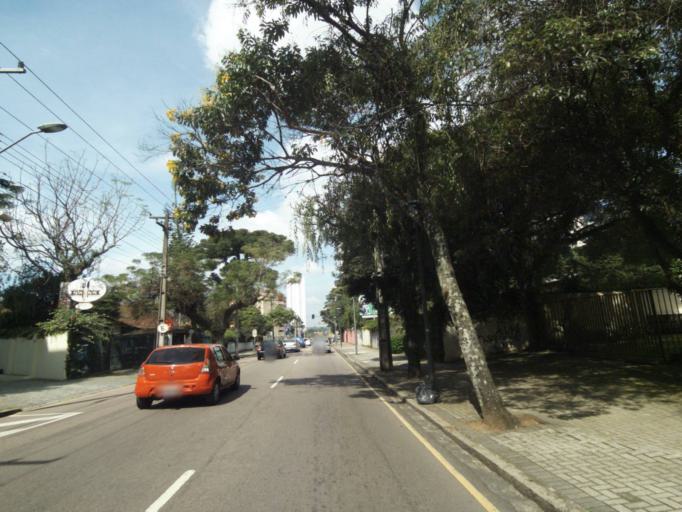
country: BR
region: Parana
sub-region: Curitiba
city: Curitiba
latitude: -25.4310
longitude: -49.2573
